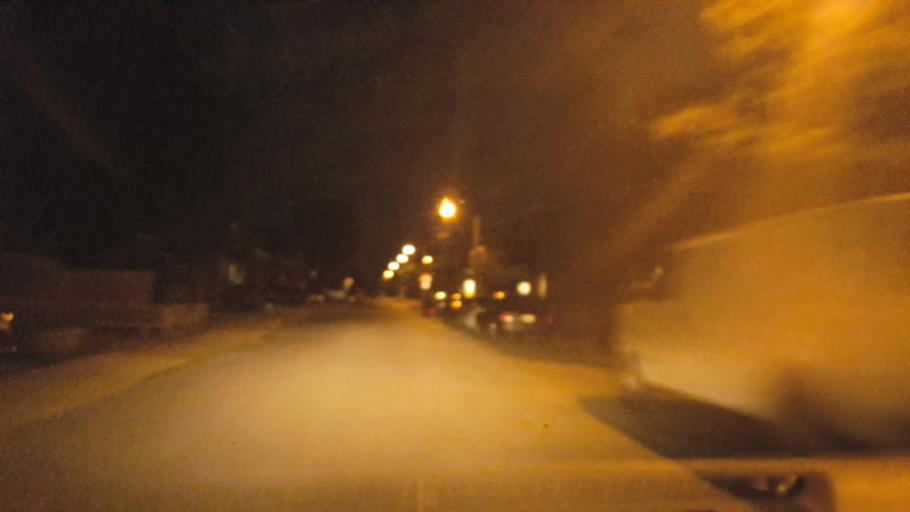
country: CA
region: Ontario
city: Ottawa
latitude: 45.4079
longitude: -75.7081
